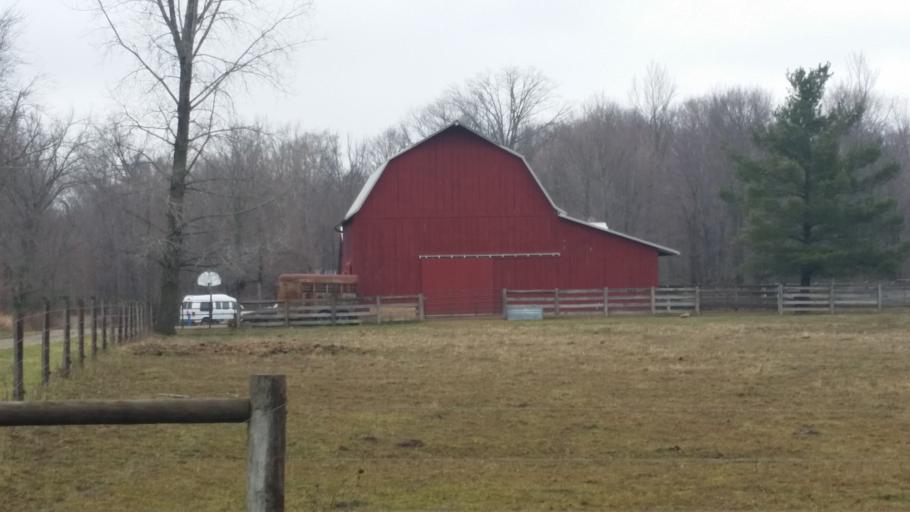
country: US
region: Ohio
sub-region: Morrow County
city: Mount Gilead
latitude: 40.4581
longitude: -82.7128
